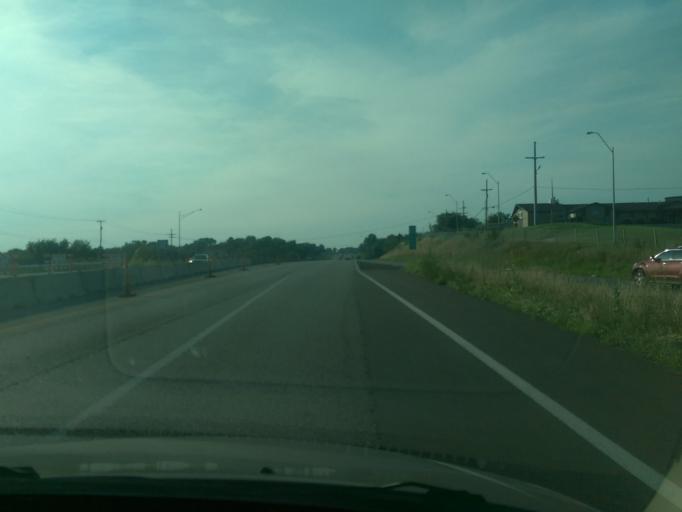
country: US
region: Missouri
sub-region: Platte County
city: Riverside
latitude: 39.2116
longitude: -94.6395
